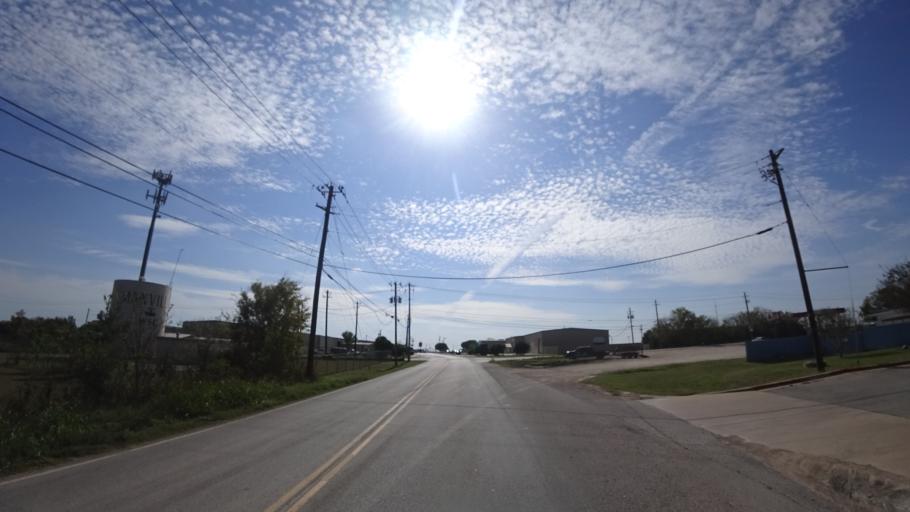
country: US
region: Texas
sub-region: Travis County
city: Pflugerville
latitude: 30.4063
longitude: -97.6280
